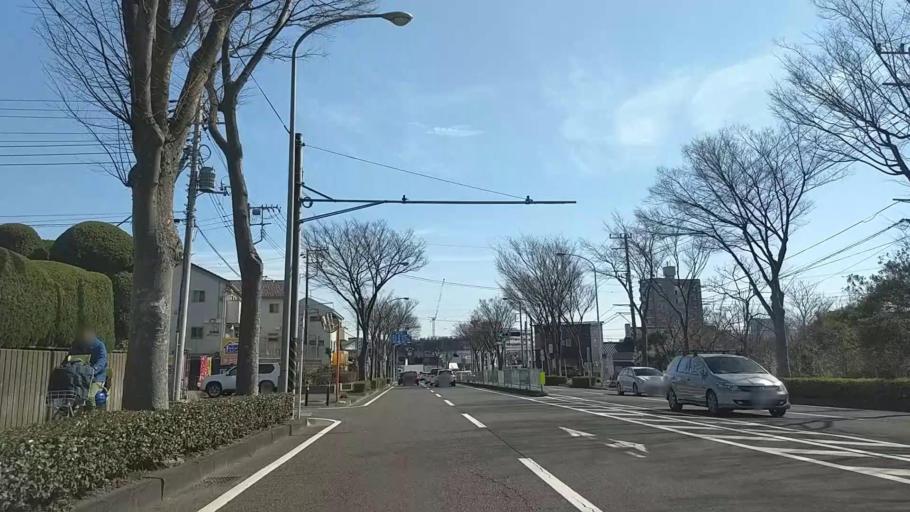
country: JP
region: Kanagawa
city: Fujisawa
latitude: 35.3472
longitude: 139.4477
